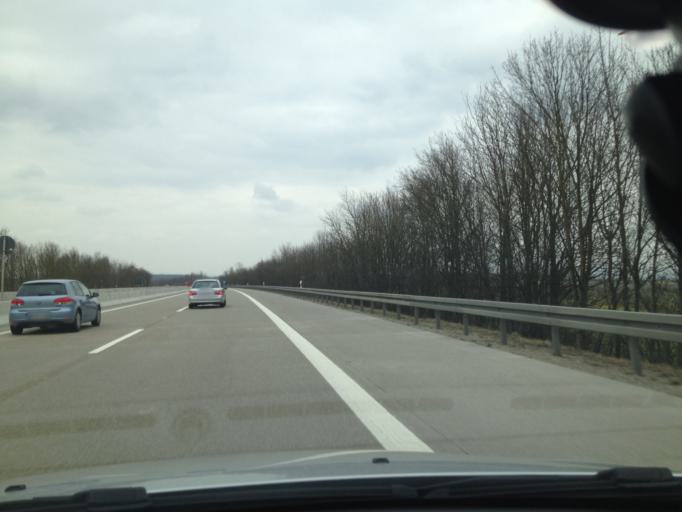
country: DE
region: Bavaria
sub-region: Regierungsbezirk Mittelfranken
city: Gollhofen
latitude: 49.5957
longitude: 10.1747
